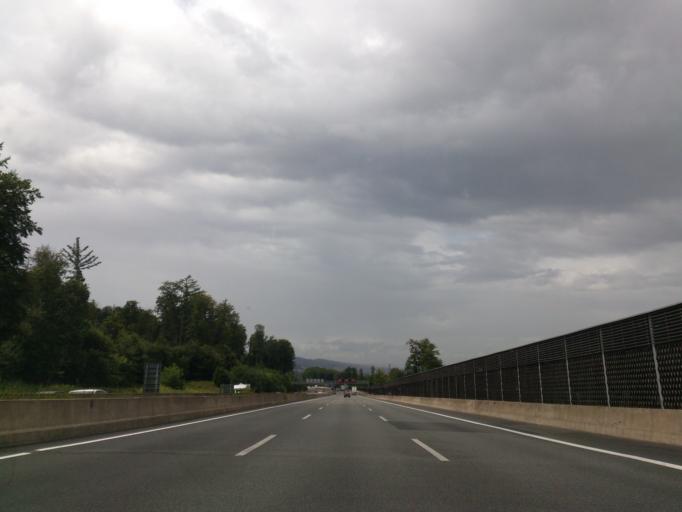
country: DE
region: Lower Saxony
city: Buchholz
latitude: 52.2185
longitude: 9.1570
